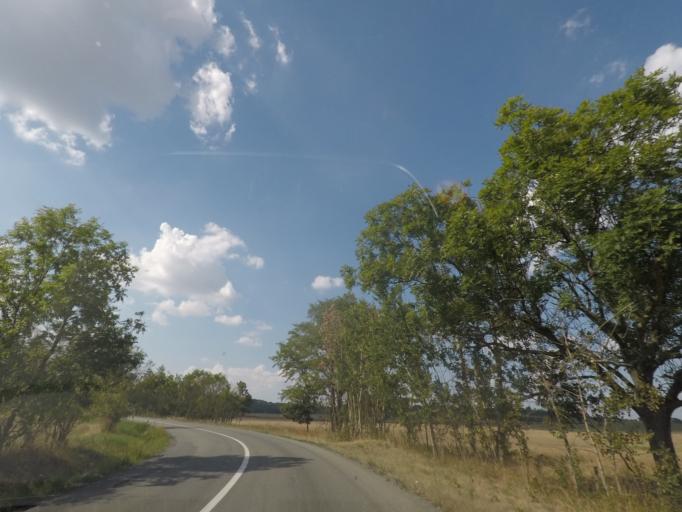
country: CZ
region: Kralovehradecky
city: Trebechovice pod Orebem
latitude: 50.2156
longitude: 15.9885
